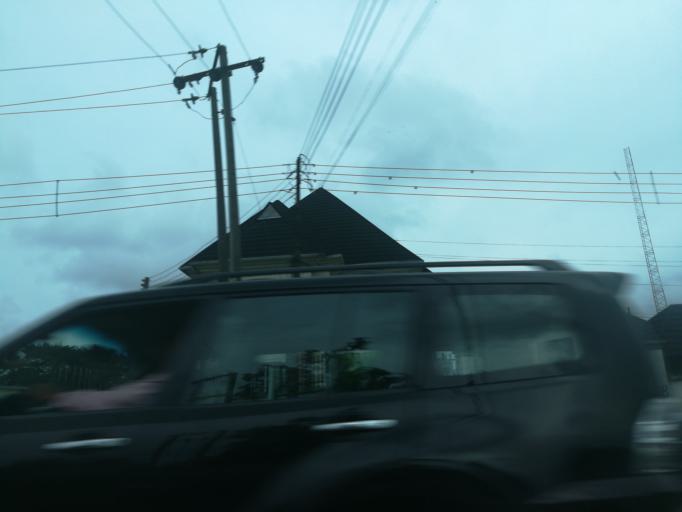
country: NG
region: Rivers
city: Port Harcourt
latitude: 4.8164
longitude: 6.9997
